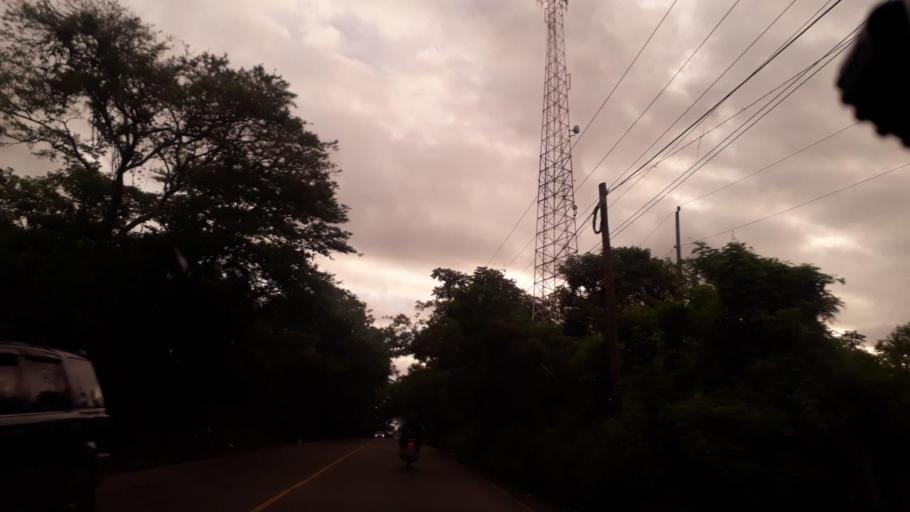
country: GT
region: Jutiapa
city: El Progreso
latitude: 14.3188
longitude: -89.8641
